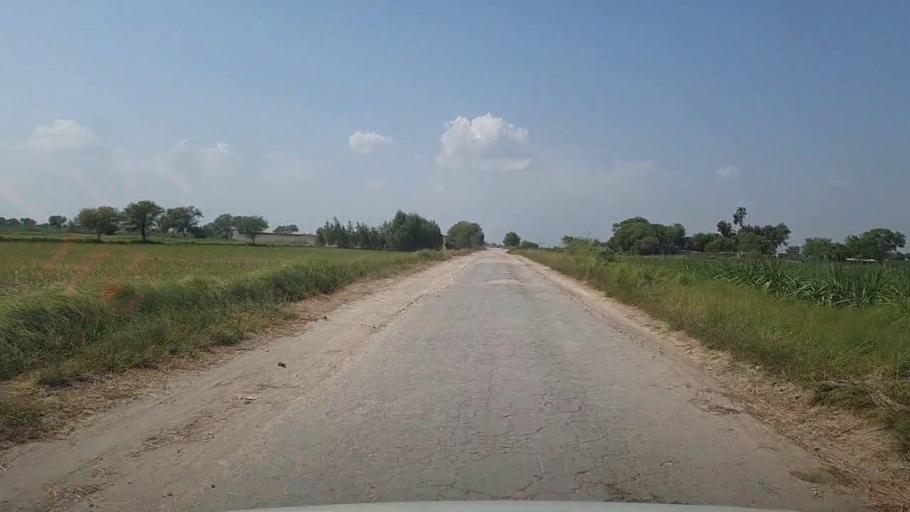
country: PK
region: Sindh
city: Khairpur
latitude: 28.0913
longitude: 69.6307
